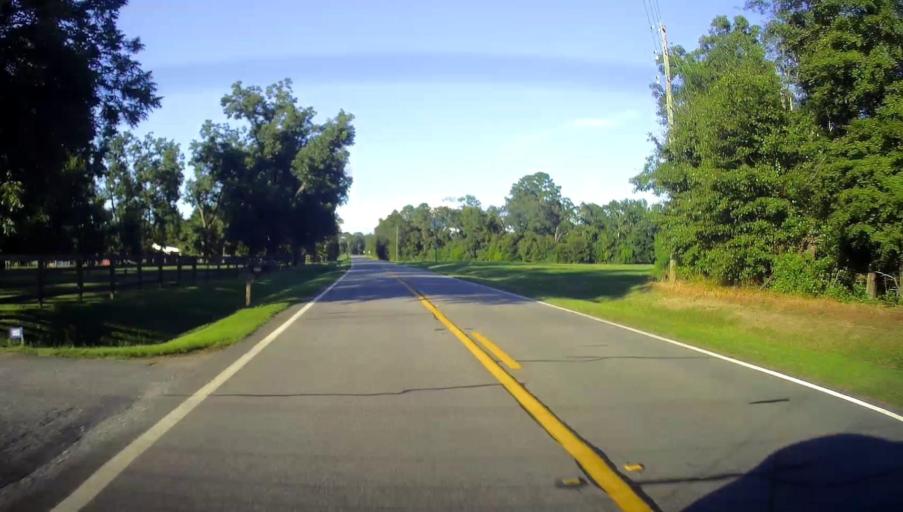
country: US
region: Georgia
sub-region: Pulaski County
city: Hawkinsville
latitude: 32.2722
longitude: -83.5040
